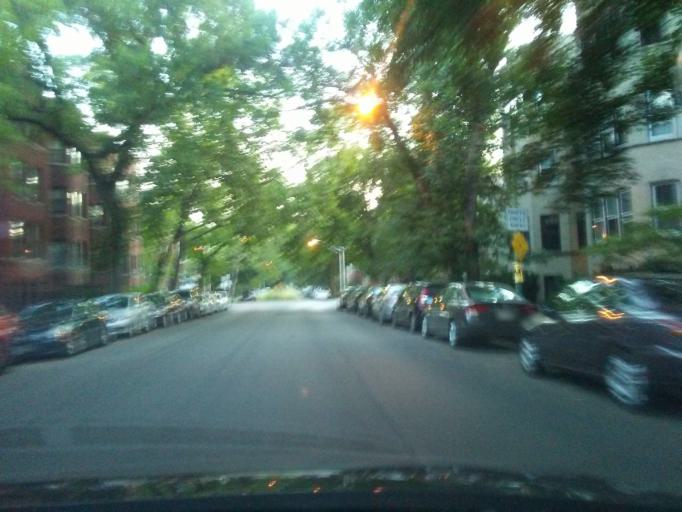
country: US
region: Illinois
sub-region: Cook County
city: Evanston
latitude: 42.0011
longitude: -87.6704
